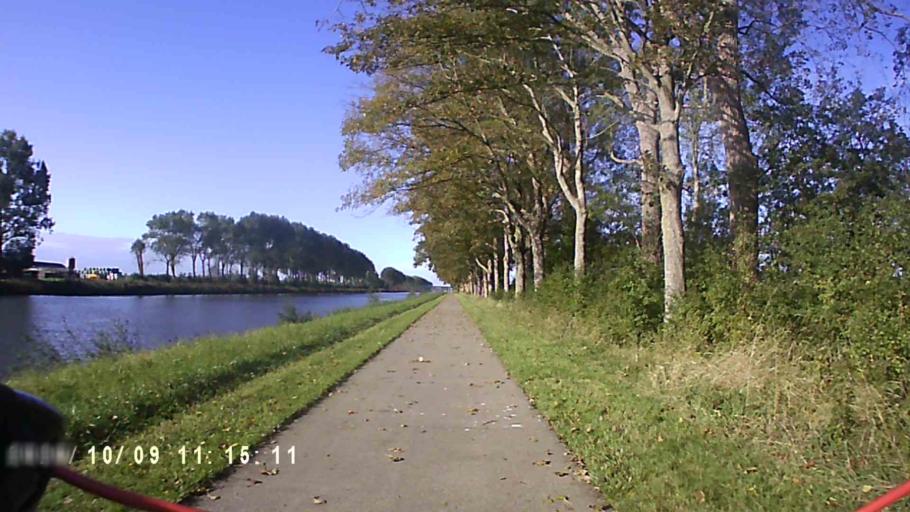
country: NL
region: Groningen
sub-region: Gemeente Zuidhorn
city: Aduard
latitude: 53.2601
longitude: 6.4331
